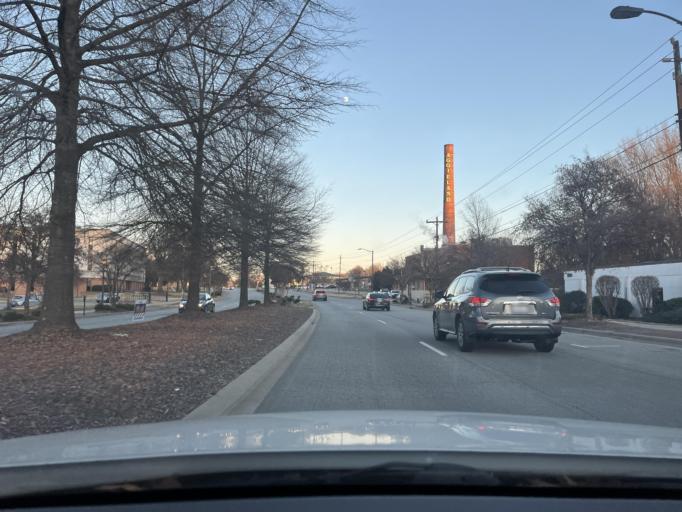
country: US
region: North Carolina
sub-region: Guilford County
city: Greensboro
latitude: 36.0714
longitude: -79.7758
